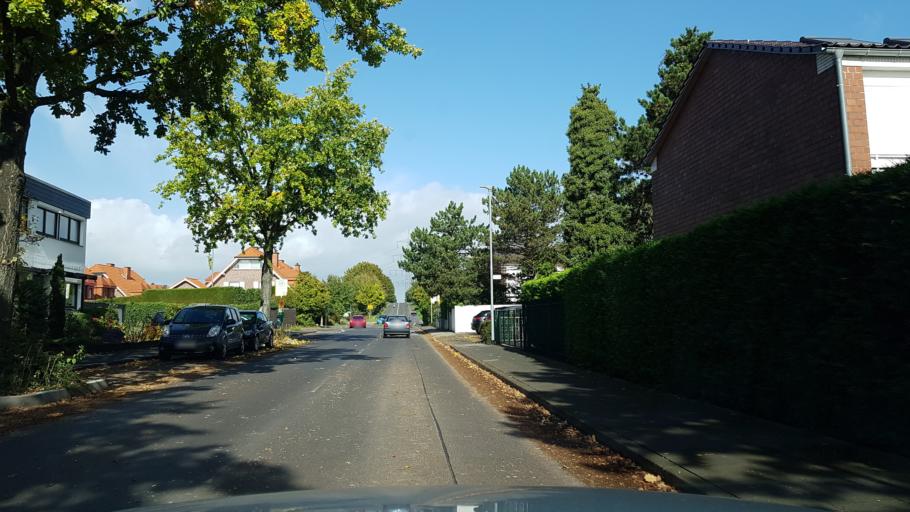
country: DE
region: North Rhine-Westphalia
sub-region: Regierungsbezirk Dusseldorf
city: Kaarst
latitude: 51.2327
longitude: 6.6274
